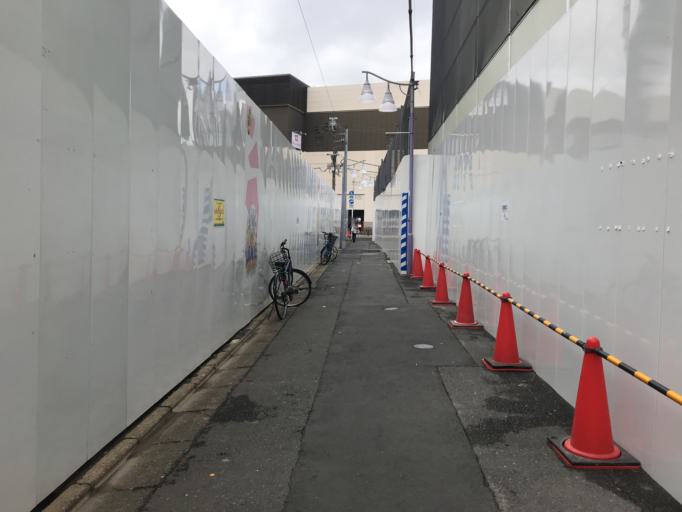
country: JP
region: Tokyo
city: Tokyo
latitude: 35.6203
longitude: 139.7054
